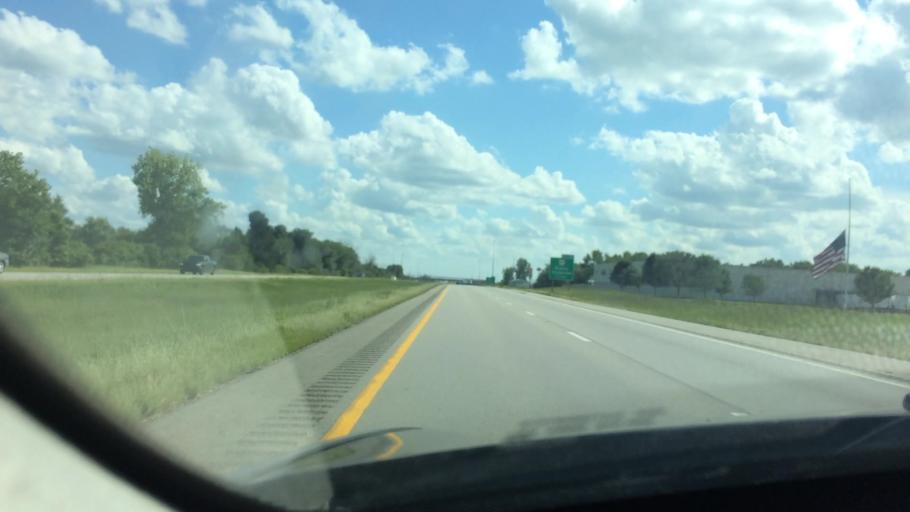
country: US
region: Ohio
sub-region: Shelby County
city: Sidney
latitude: 40.2981
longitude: -84.1813
